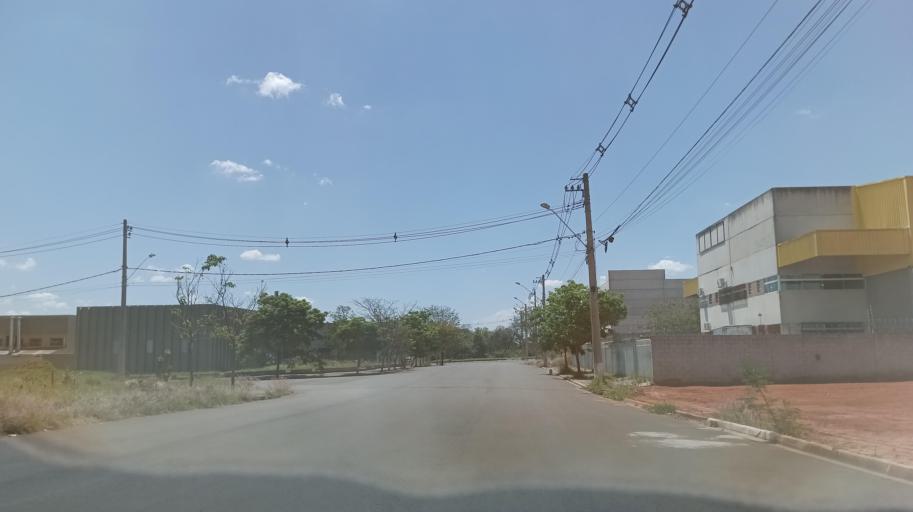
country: BR
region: Sao Paulo
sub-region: Sorocaba
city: Sorocaba
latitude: -23.4661
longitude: -47.4546
